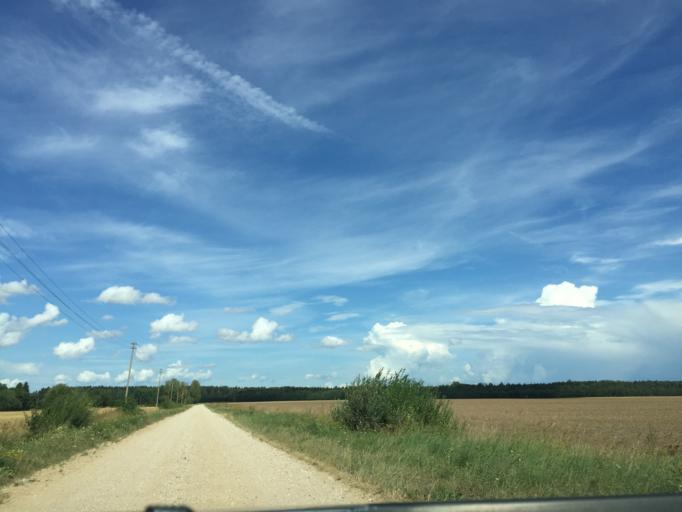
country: LT
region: Siauliu apskritis
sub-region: Joniskis
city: Joniskis
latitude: 56.3508
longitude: 23.6269
